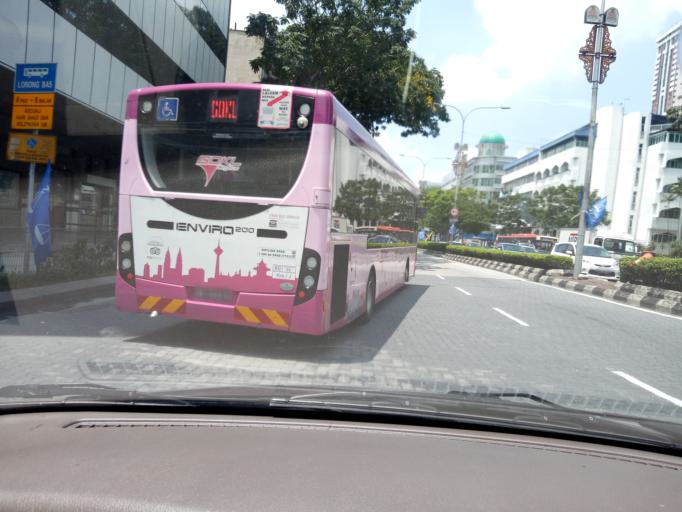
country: MY
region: Kuala Lumpur
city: Kuala Lumpur
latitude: 3.1715
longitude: 101.6929
